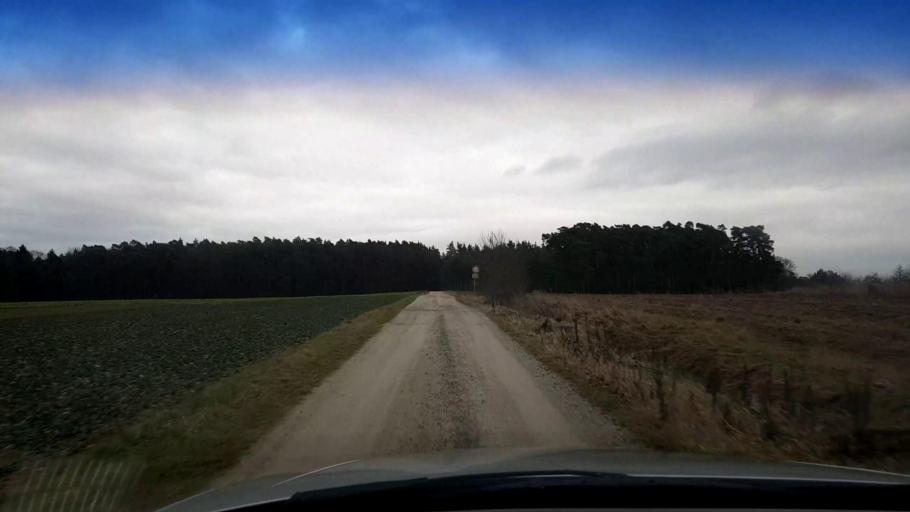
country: DE
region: Bavaria
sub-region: Upper Franconia
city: Lauter
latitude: 49.9471
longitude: 10.7774
